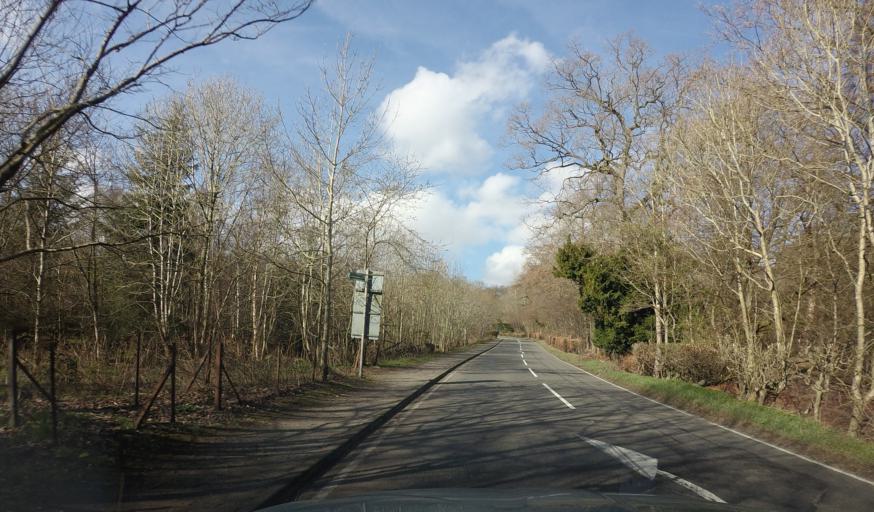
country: GB
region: Scotland
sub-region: Midlothian
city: Penicuik
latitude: 55.8279
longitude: -3.2368
